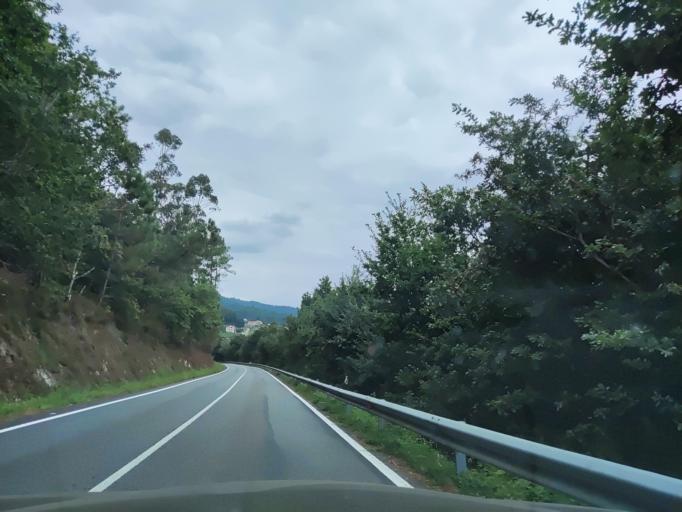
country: ES
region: Galicia
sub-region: Provincia da Coruna
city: Teo
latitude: 42.7527
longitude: -8.5598
